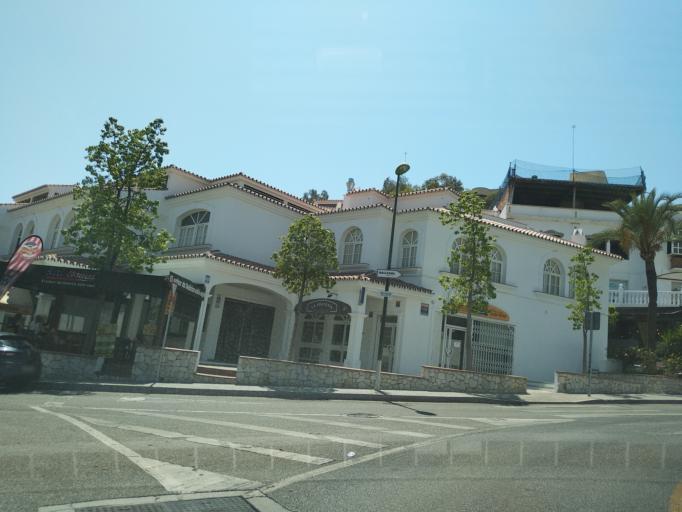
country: ES
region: Andalusia
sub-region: Provincia de Malaga
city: Malaga
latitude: 36.7267
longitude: -4.3819
